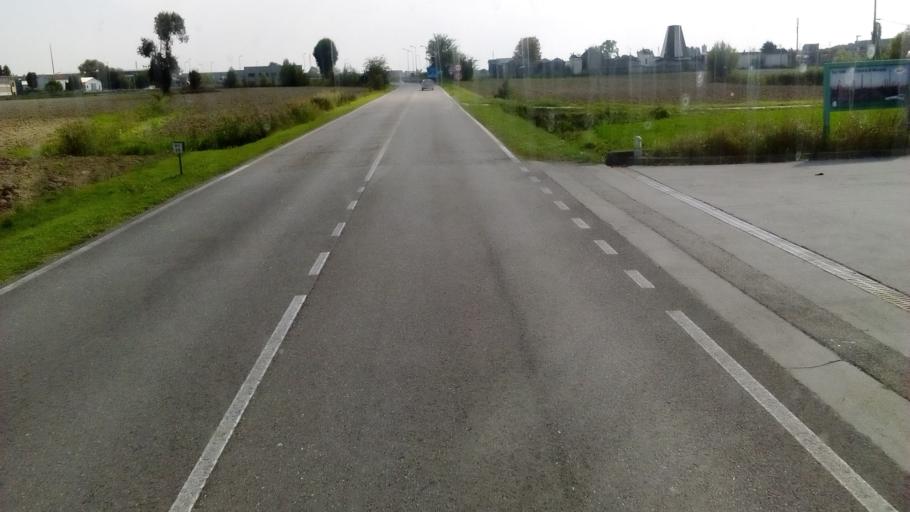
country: IT
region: Veneto
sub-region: Provincia di Rovigo
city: Calto
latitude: 44.9979
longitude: 11.3577
